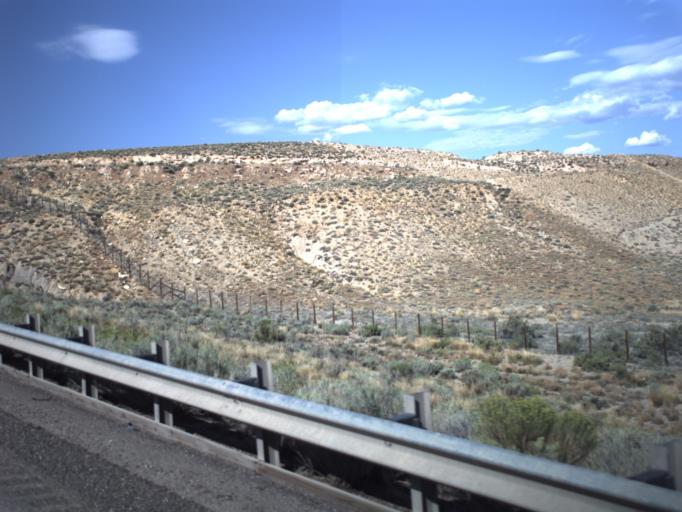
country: US
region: Utah
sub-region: Emery County
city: Huntington
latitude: 39.4079
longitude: -110.8836
